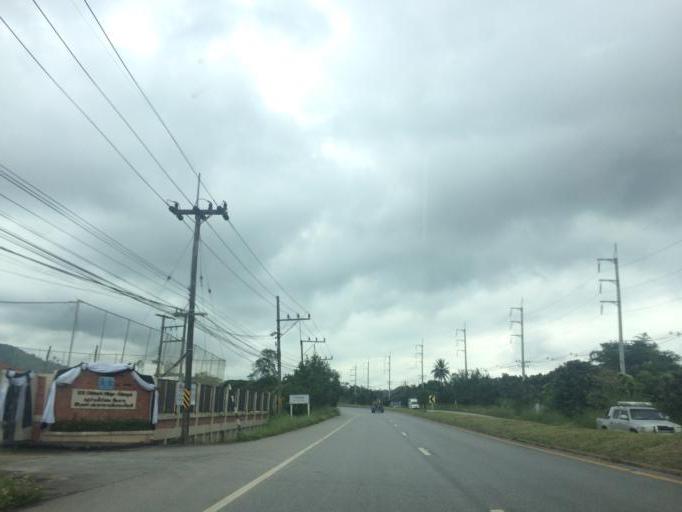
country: TH
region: Chiang Rai
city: Mae Chan
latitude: 20.0893
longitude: 99.8748
